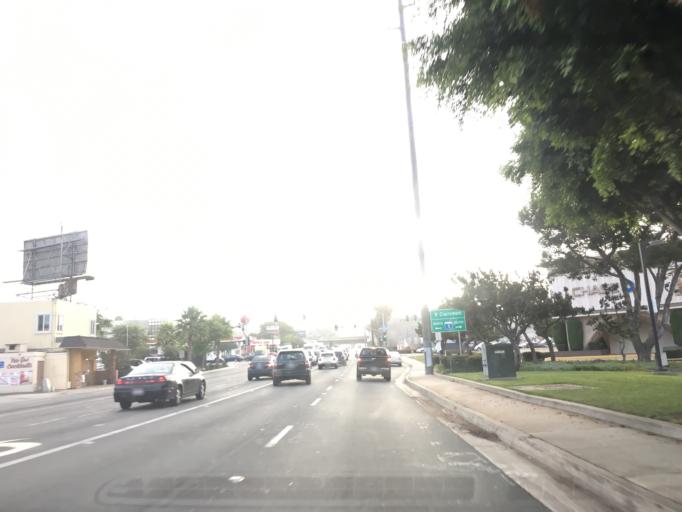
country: US
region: California
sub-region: San Diego County
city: La Jolla
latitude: 32.8058
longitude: -117.2202
